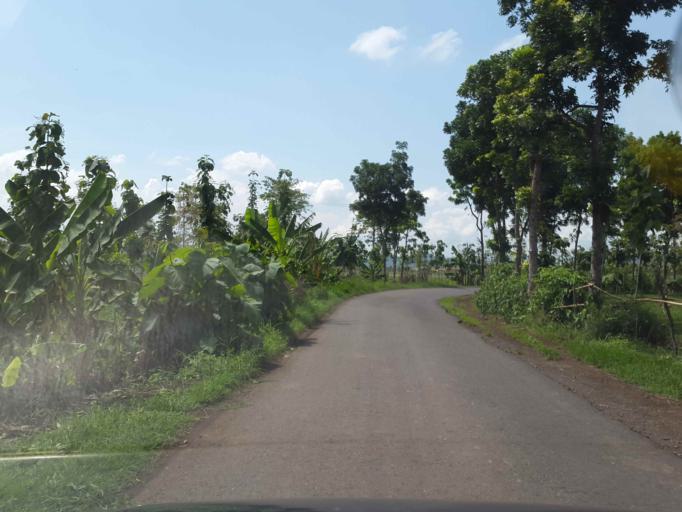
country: ID
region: Central Java
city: Margasari
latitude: -7.0754
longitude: 108.9958
